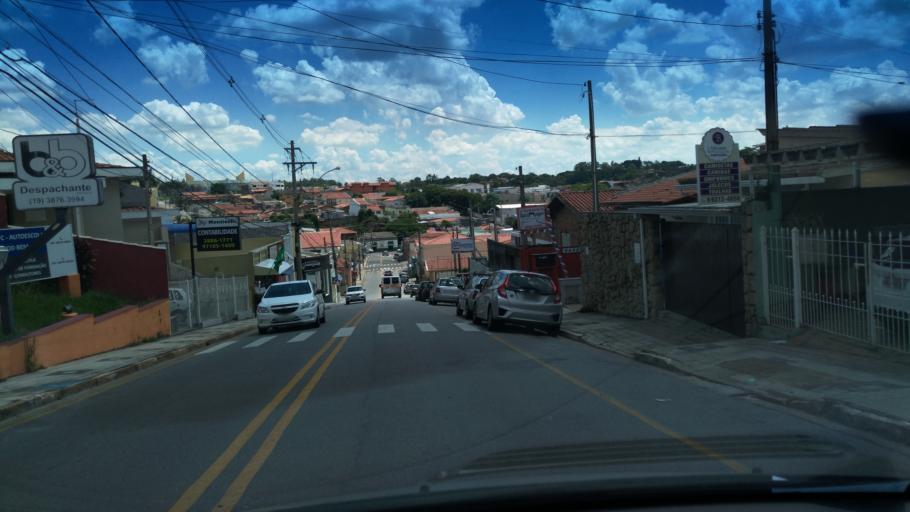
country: BR
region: Sao Paulo
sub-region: Vinhedo
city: Vinhedo
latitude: -23.0279
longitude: -46.9768
